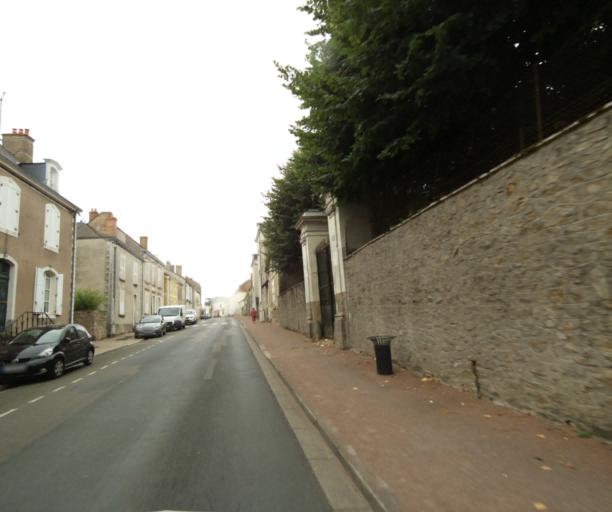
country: FR
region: Pays de la Loire
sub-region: Departement de la Sarthe
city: Sable-sur-Sarthe
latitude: 47.8368
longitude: -0.3249
